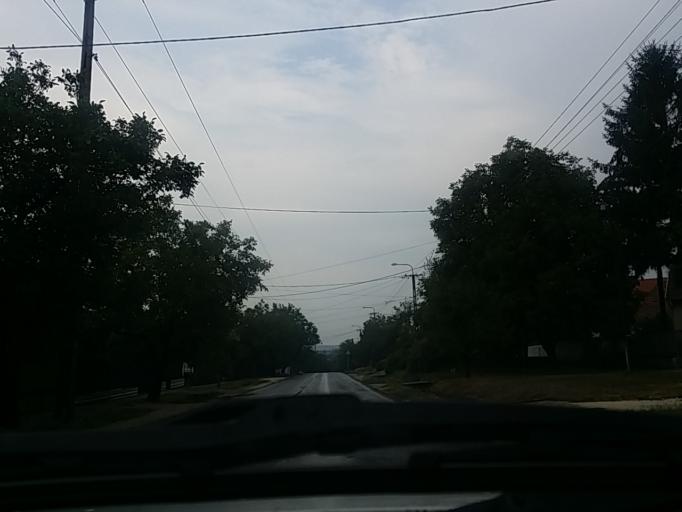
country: HU
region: Pest
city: Paty
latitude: 47.5123
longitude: 18.8388
